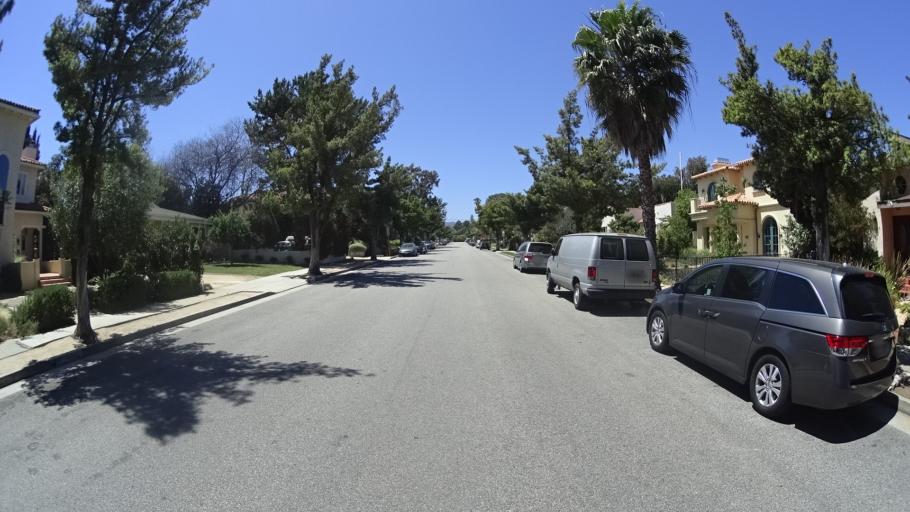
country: US
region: California
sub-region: Los Angeles County
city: Santa Monica
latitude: 34.0369
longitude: -118.4842
